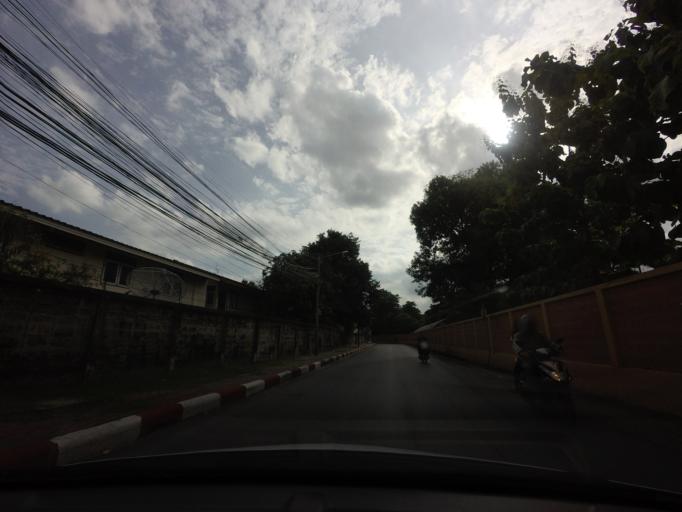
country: TH
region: Bangkok
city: Chatuchak
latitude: 13.8528
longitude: 100.5783
